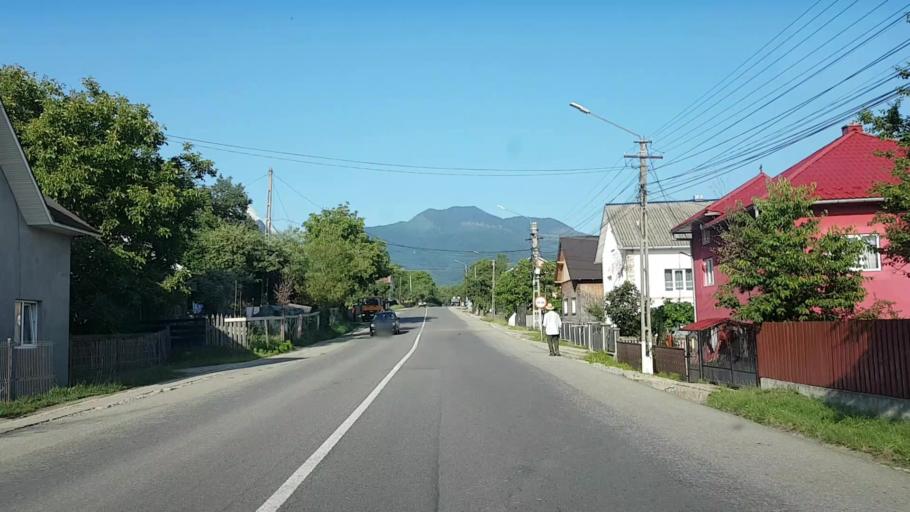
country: RO
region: Bistrita-Nasaud
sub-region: Comuna Tiha Bargaului
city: Tiha Bargaului
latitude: 47.2297
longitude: 24.7818
